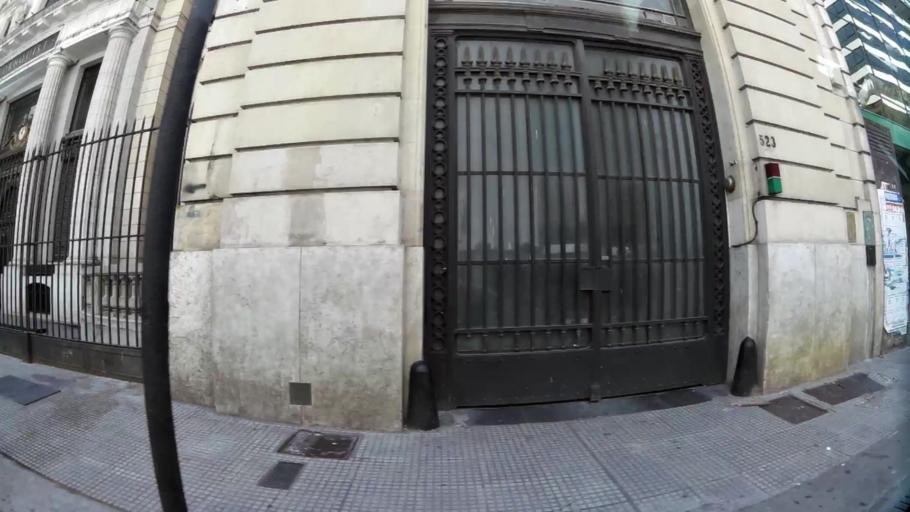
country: AR
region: Buenos Aires F.D.
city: Buenos Aires
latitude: -34.6069
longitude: -58.3743
